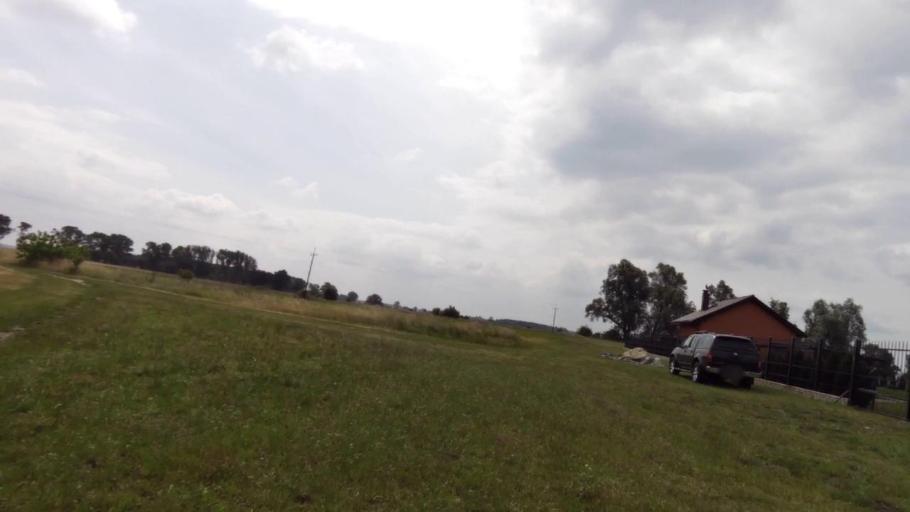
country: PL
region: West Pomeranian Voivodeship
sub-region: Powiat goleniowski
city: Goleniow
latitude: 53.4991
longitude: 14.7055
